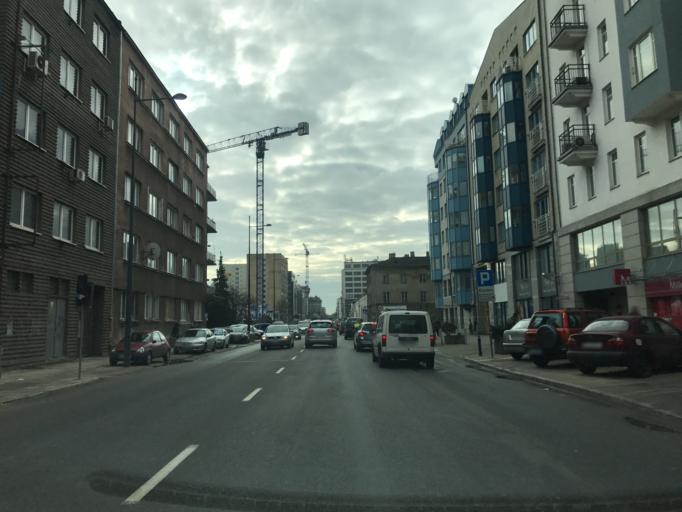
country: PL
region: Masovian Voivodeship
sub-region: Warszawa
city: Wola
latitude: 52.2338
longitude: 20.9912
